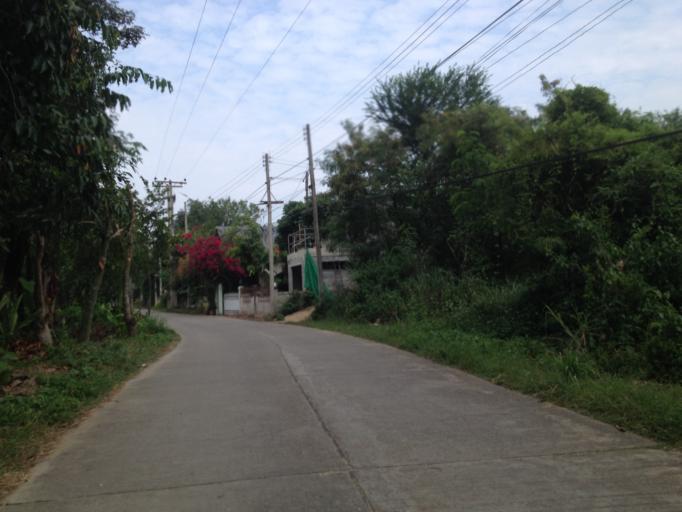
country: TH
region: Chiang Mai
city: Hang Dong
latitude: 18.6735
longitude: 98.9013
